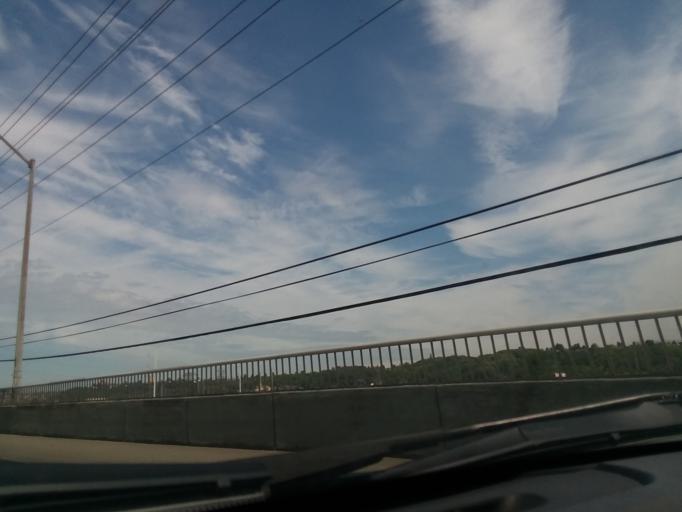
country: US
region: Washington
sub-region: King County
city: Seattle
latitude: 47.5630
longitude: -122.3343
